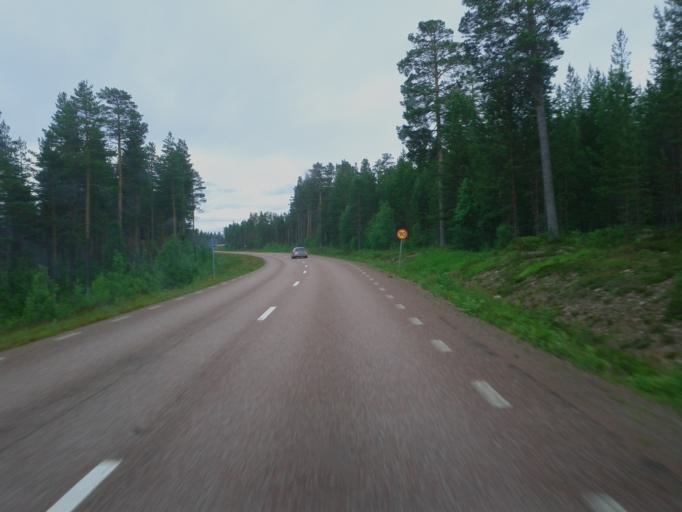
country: SE
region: Dalarna
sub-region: Alvdalens Kommun
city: AElvdalen
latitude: 61.5443
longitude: 13.3375
